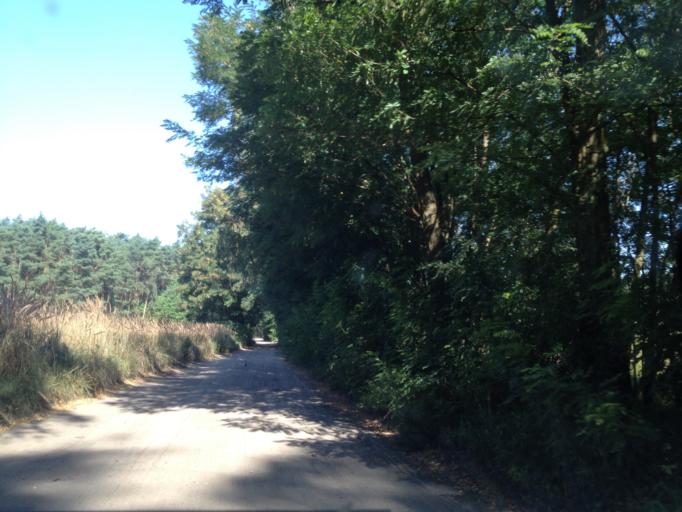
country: PL
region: Greater Poland Voivodeship
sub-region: Powiat sredzki
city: Zaniemysl
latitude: 52.1072
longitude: 17.1265
